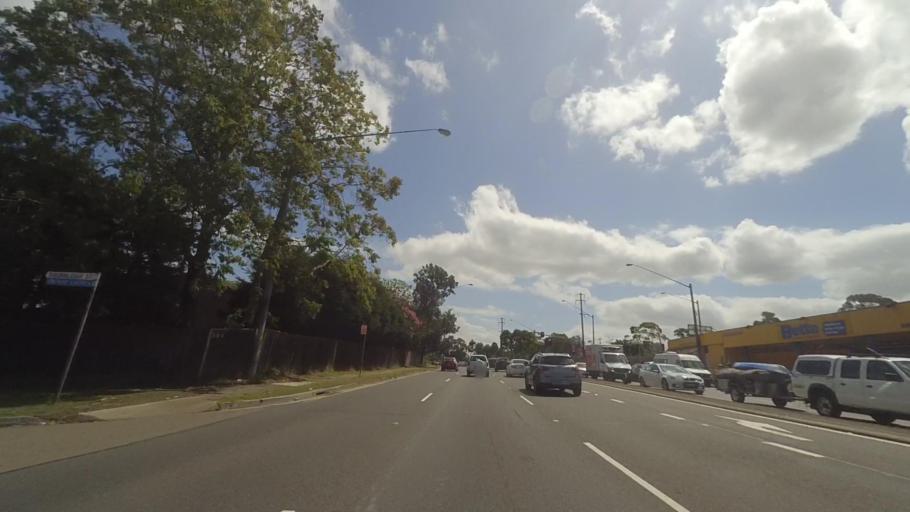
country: AU
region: New South Wales
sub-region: Hornsby Shire
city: Pennant Hills
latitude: -33.7325
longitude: 151.0786
